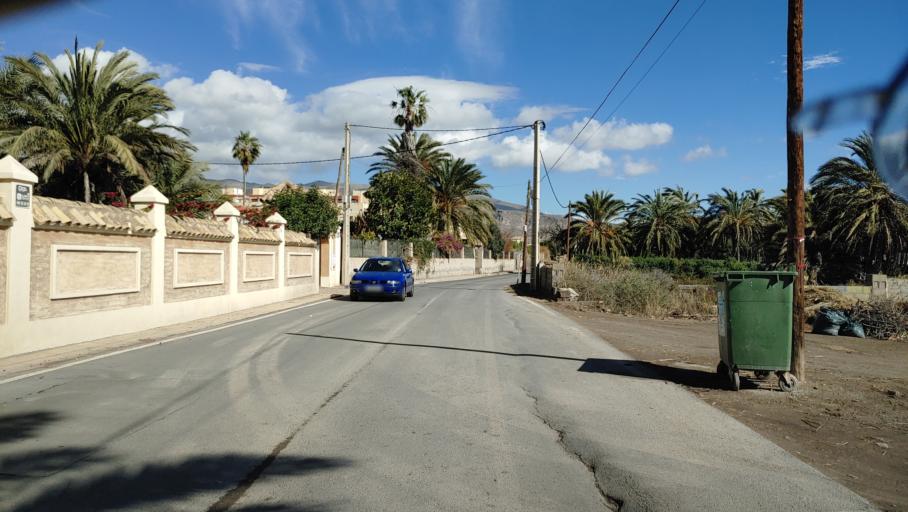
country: ES
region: Andalusia
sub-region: Provincia de Almeria
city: Aguadulce
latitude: 36.7934
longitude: -2.5868
